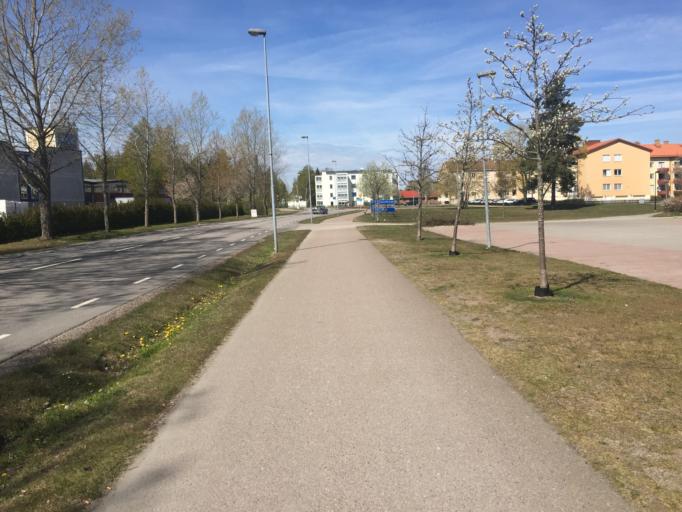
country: SE
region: Kalmar
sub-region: Nybro Kommun
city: Nybro
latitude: 56.7439
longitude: 15.8997
